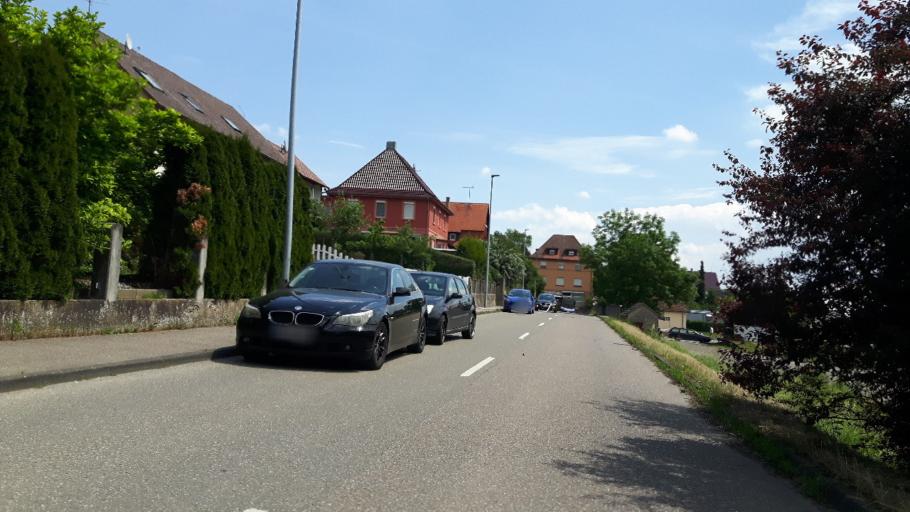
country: DE
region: Baden-Wuerttemberg
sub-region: Regierungsbezirk Stuttgart
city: Neuenstadt am Kocher
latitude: 49.2392
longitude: 9.3598
